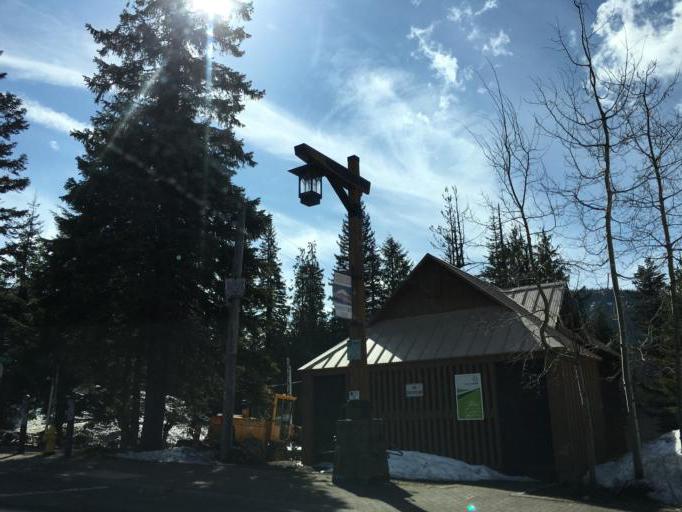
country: US
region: Oregon
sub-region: Clackamas County
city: Mount Hood Village
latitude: 45.3040
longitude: -121.7552
